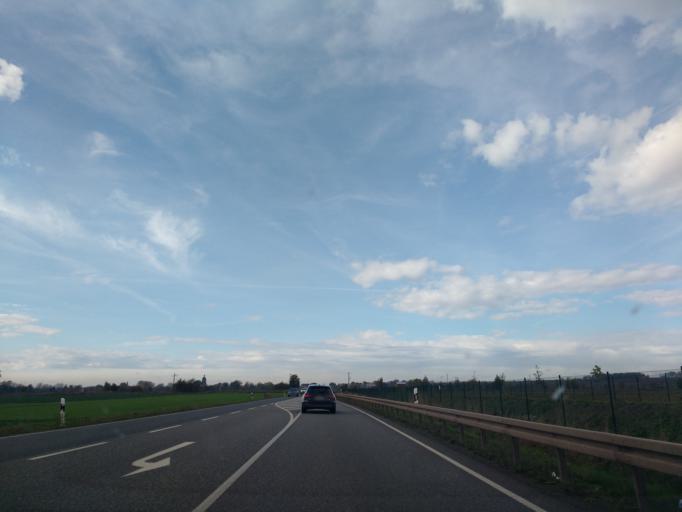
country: DE
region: Thuringia
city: Heringen
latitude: 51.4808
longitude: 10.8613
